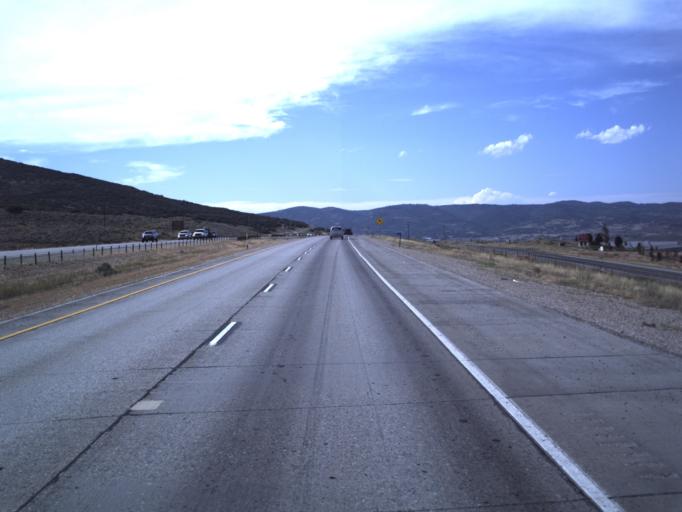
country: US
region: Utah
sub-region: Summit County
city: Park City
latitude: 40.6919
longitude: -111.4680
